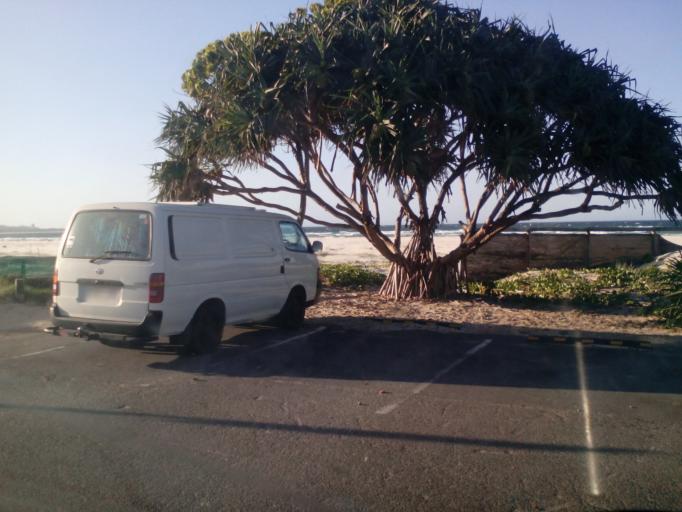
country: AU
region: New South Wales
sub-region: Tweed
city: Kingscliff
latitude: -28.2576
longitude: 153.5829
